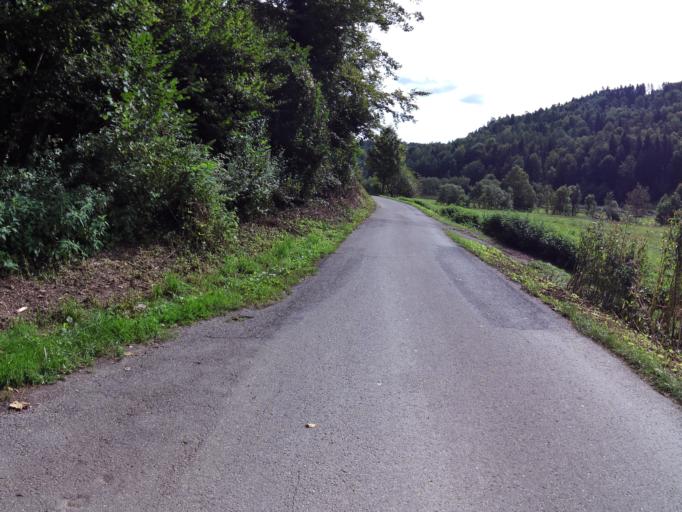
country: DE
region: Baden-Wuerttemberg
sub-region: Freiburg Region
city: Oberndorf
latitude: 48.3305
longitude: 8.5896
